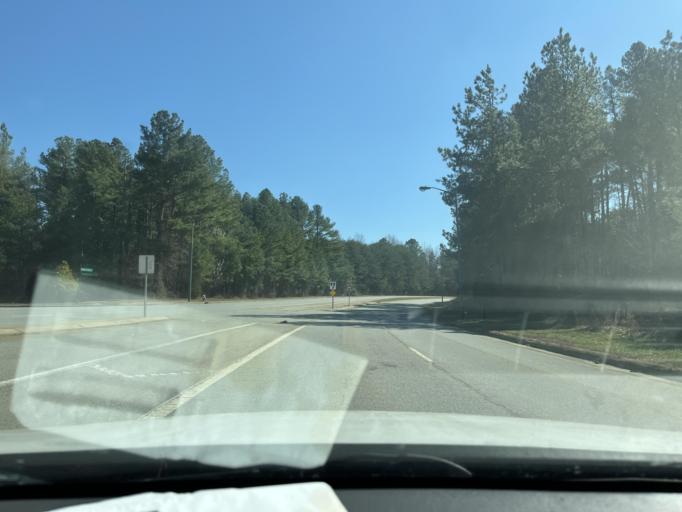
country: US
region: North Carolina
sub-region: Guilford County
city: Jamestown
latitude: 35.9925
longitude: -79.9027
